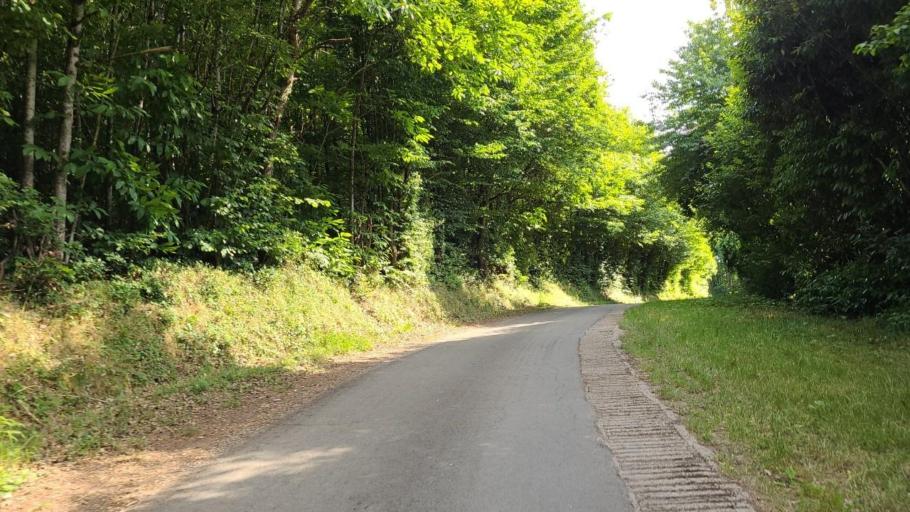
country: FR
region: Centre
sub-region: Departement d'Indre-et-Loire
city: Reugny
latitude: 47.4789
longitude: 0.8904
